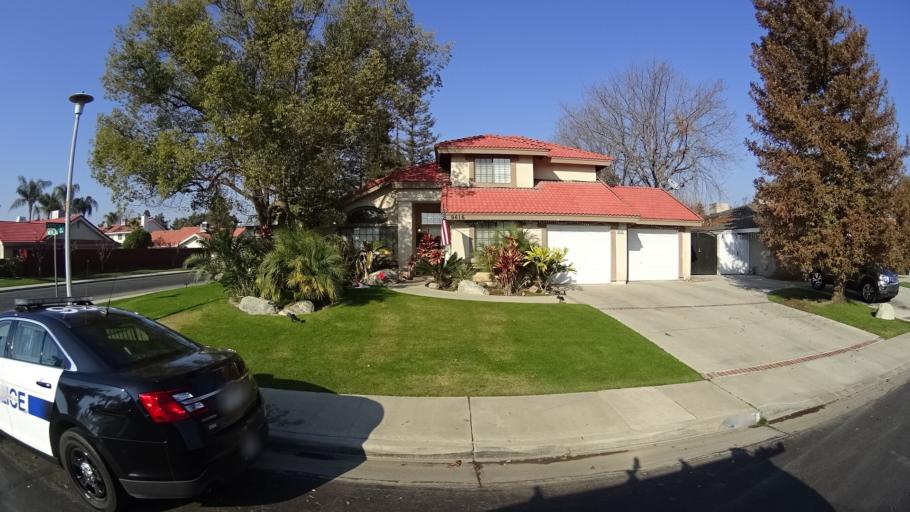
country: US
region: California
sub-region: Kern County
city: Greenacres
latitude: 35.3383
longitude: -119.1100
